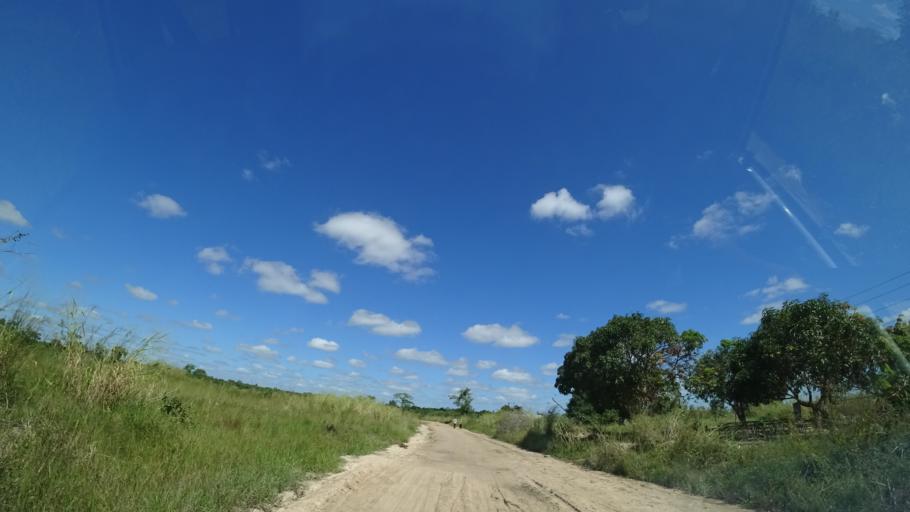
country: MZ
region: Sofala
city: Dondo
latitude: -19.3143
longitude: 34.6912
